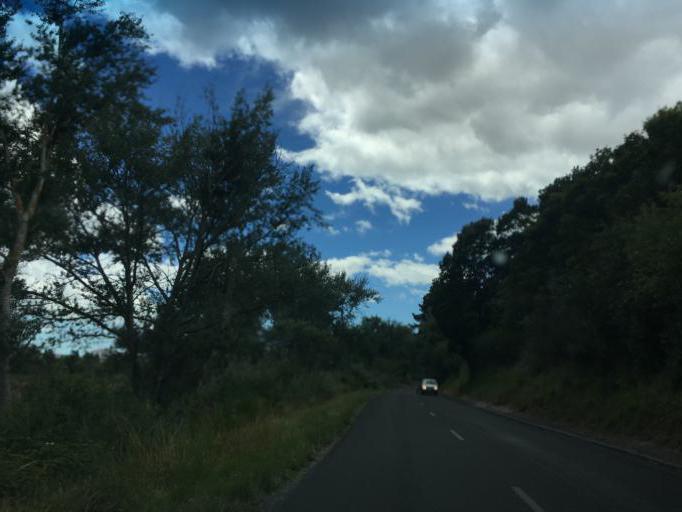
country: NZ
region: Hawke's Bay
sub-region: Hastings District
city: Hastings
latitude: -39.7348
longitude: 176.9021
